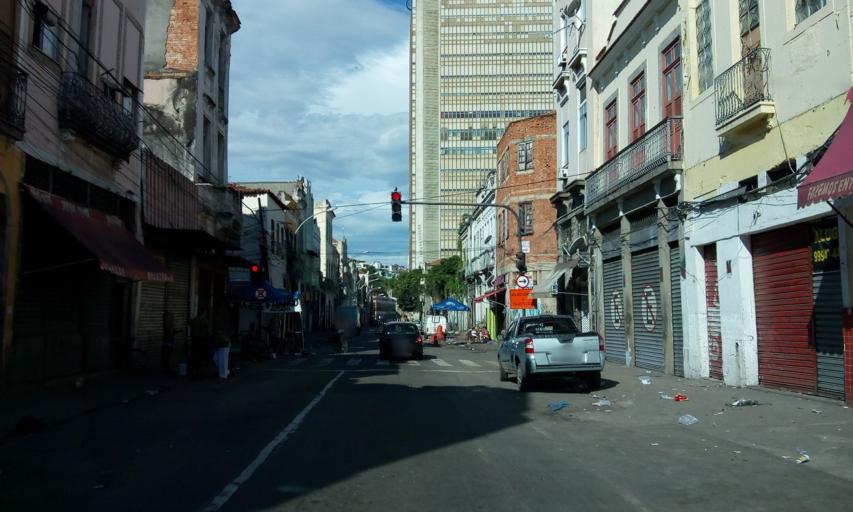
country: BR
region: Rio de Janeiro
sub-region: Rio De Janeiro
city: Rio de Janeiro
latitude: -22.9016
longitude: -43.1898
